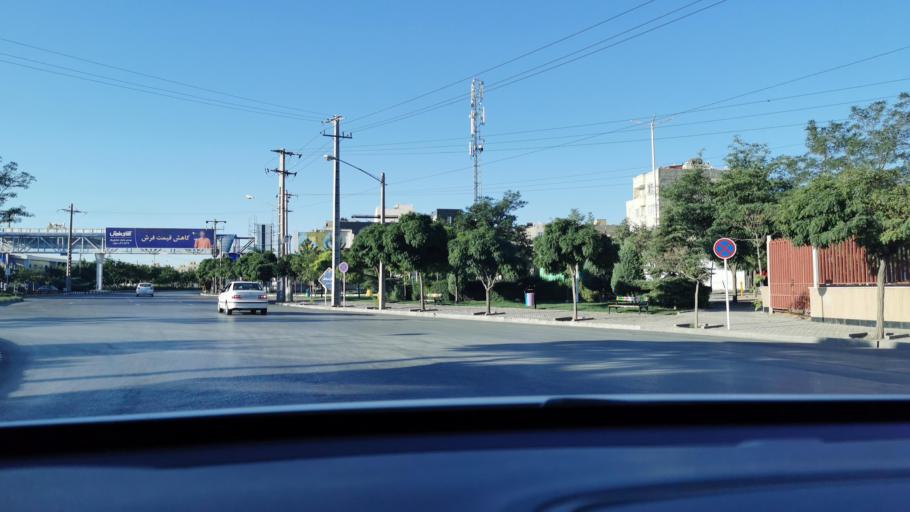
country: IR
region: Razavi Khorasan
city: Mashhad
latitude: 36.3563
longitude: 59.4876
